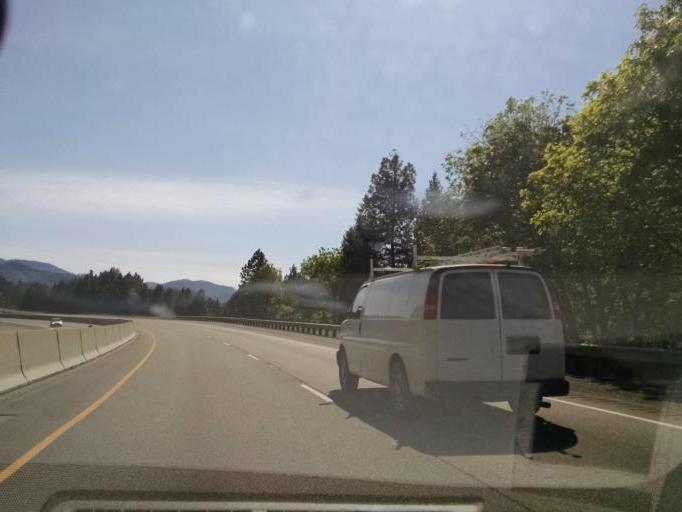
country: US
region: Oregon
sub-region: Douglas County
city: Riddle
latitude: 42.9533
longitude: -123.3296
